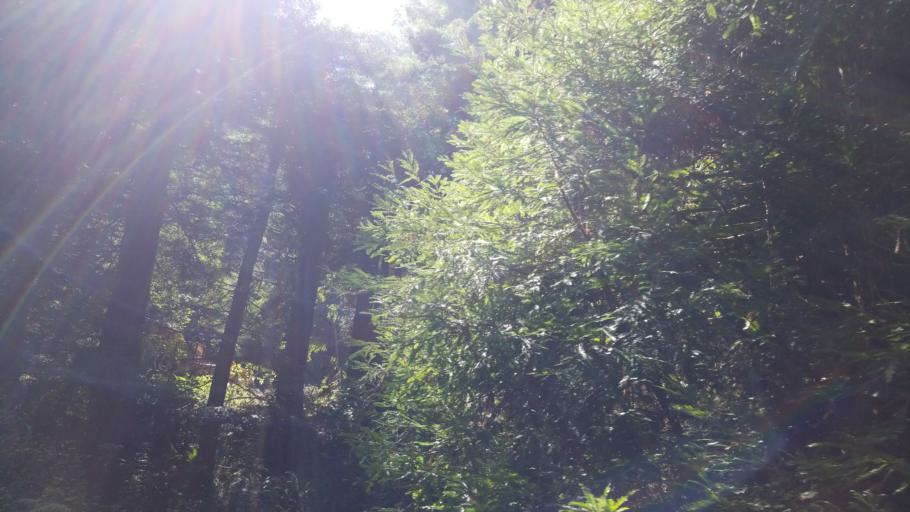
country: US
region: California
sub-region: Mendocino County
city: Fort Bragg
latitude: 39.4489
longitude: -123.7754
